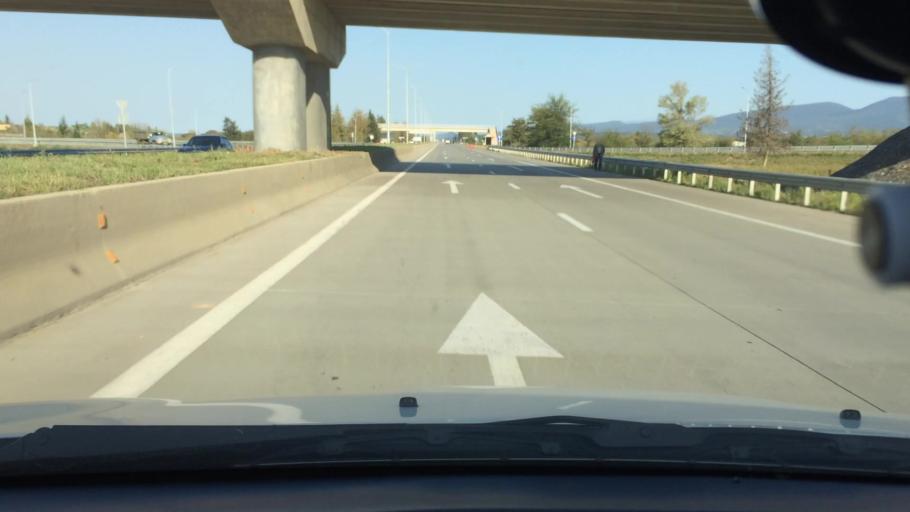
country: GE
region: Imereti
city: Zestap'oni
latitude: 42.1588
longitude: 42.9505
